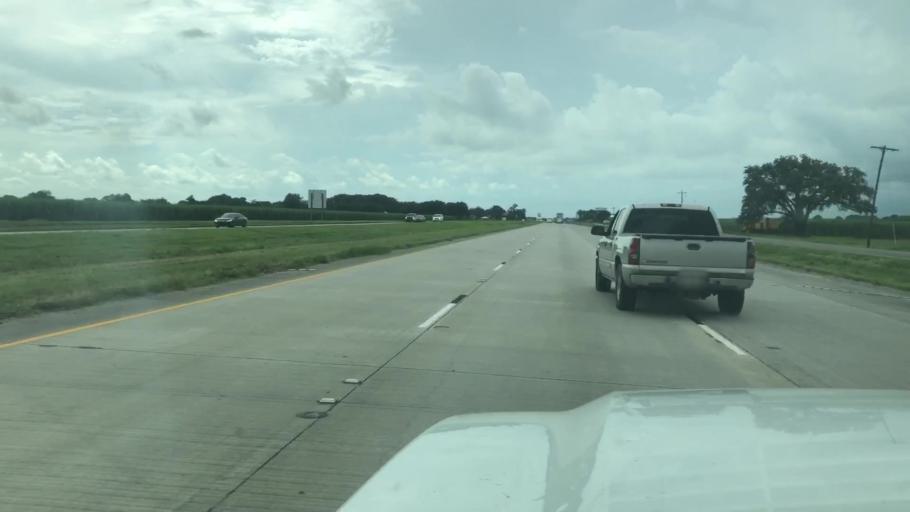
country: US
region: Louisiana
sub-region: Iberia Parish
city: Jeanerette
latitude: 29.9227
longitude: -91.7329
